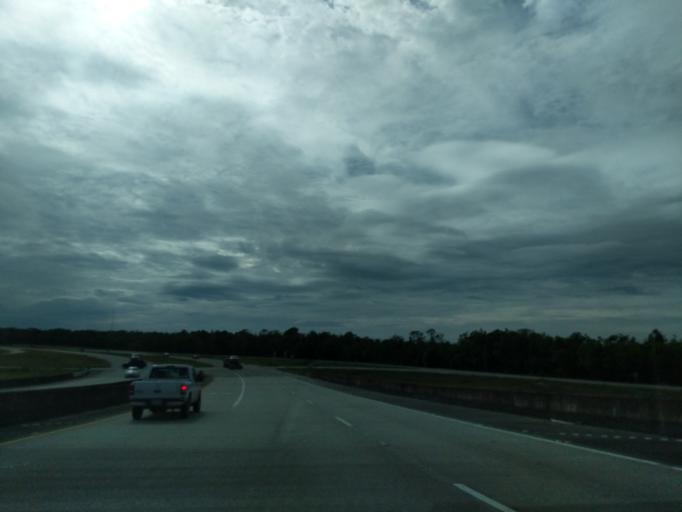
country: US
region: Louisiana
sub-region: Saint Bernard Parish
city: Chalmette
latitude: 30.0175
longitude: -89.9411
